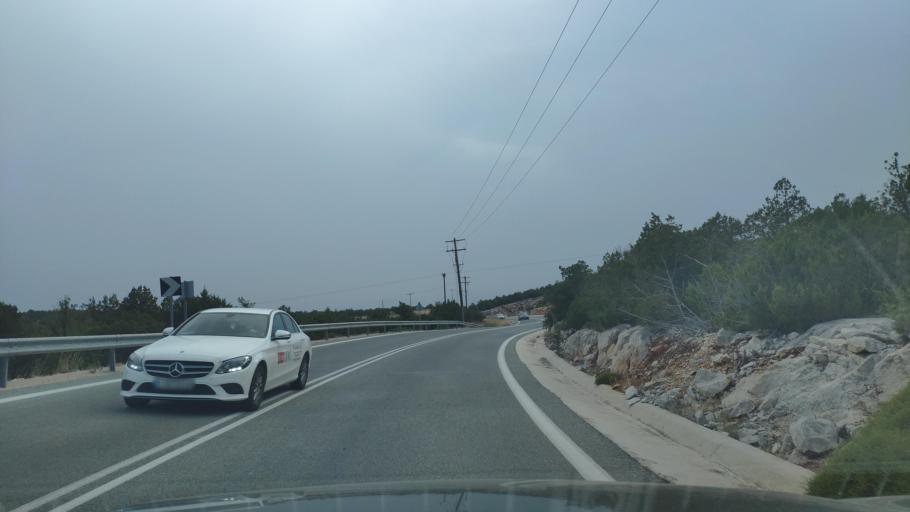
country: GR
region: Peloponnese
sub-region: Nomos Argolidos
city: Didyma
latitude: 37.4505
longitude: 23.1940
